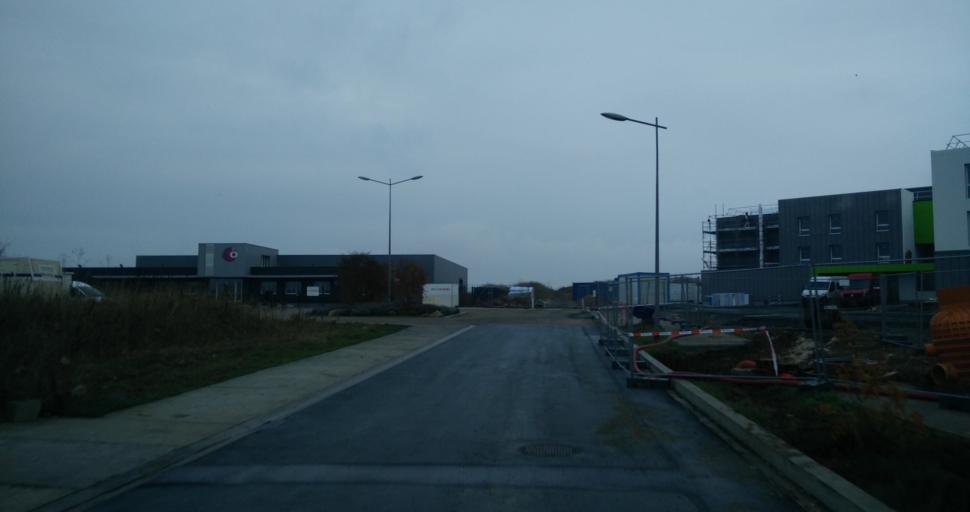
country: FR
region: Poitou-Charentes
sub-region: Departement de la Charente-Maritime
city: Nieul-sur-Mer
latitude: 46.1763
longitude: -1.2016
